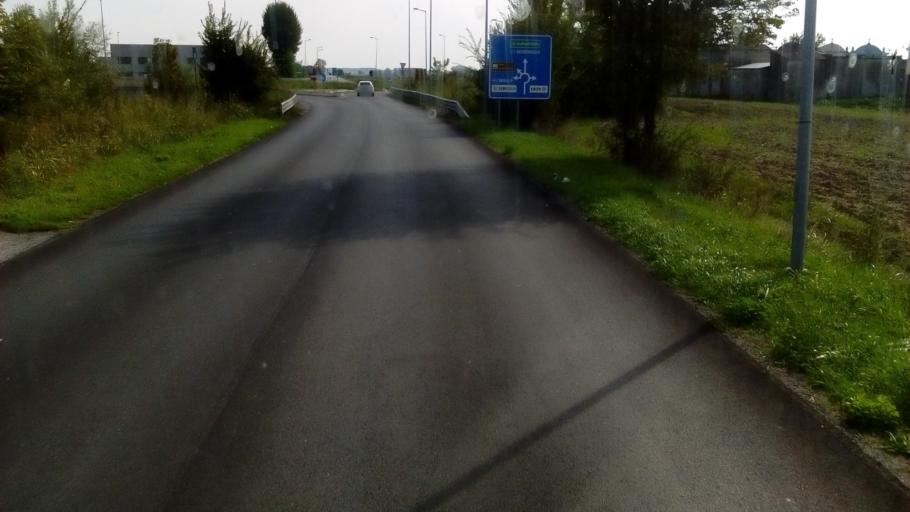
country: IT
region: Veneto
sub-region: Provincia di Rovigo
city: Calto
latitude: 44.9966
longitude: 11.3596
